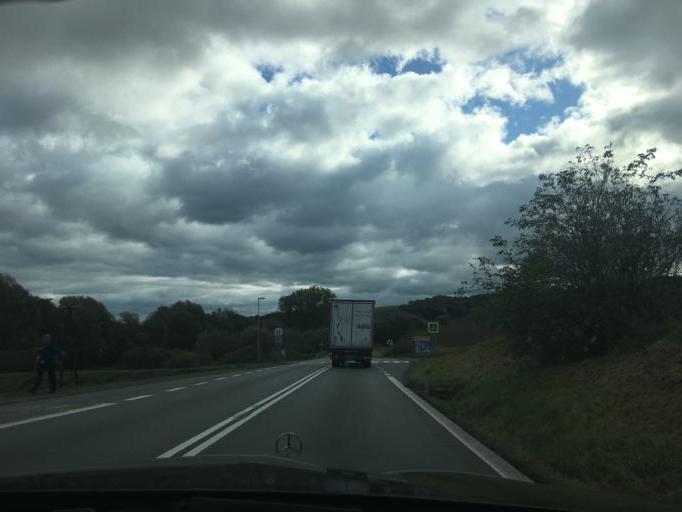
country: SK
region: Presovsky
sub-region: Okres Presov
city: Presov
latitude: 49.0446
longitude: 21.3799
